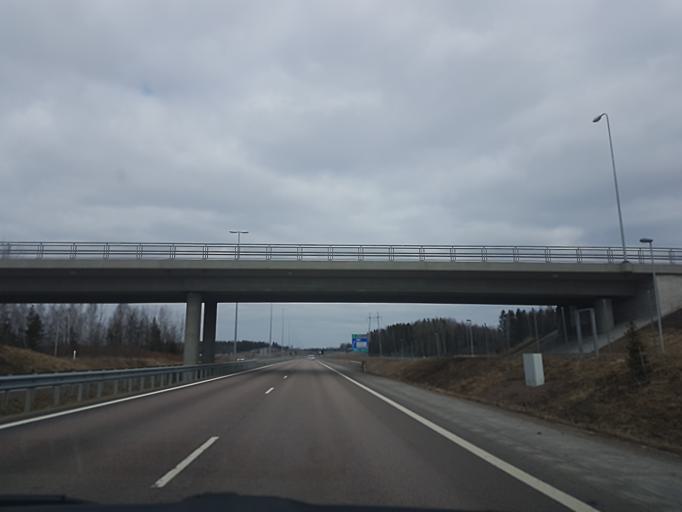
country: FI
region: Kymenlaakso
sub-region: Kotka-Hamina
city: Hamina
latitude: 60.5791
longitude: 27.1420
